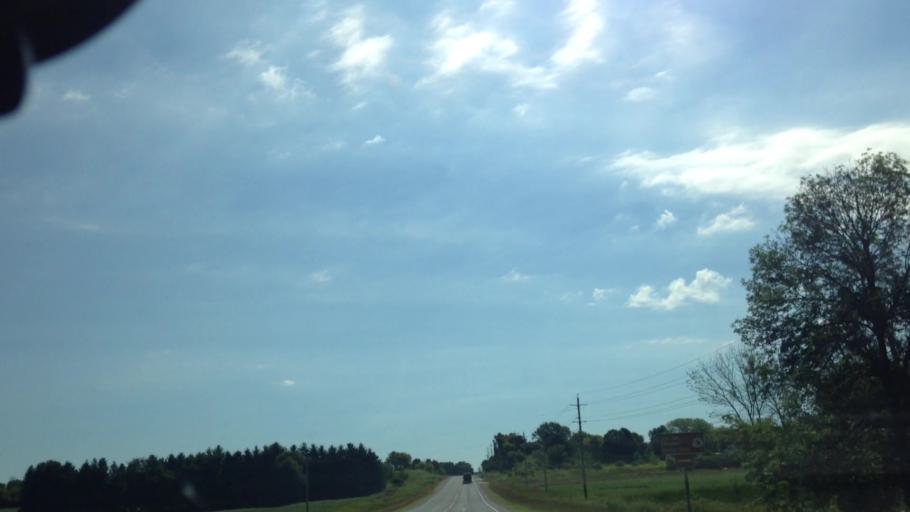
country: US
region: Wisconsin
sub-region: Washington County
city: Slinger
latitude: 43.3534
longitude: -88.2742
